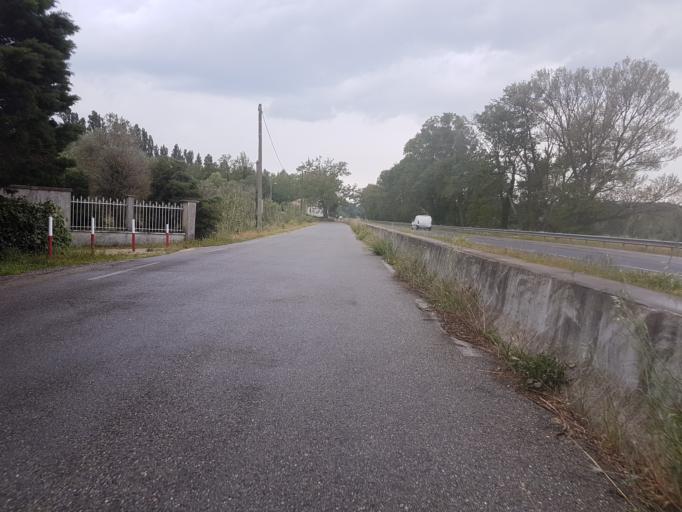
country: FR
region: Provence-Alpes-Cote d'Azur
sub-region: Departement du Vaucluse
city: Avignon
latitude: 43.9599
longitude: 4.8105
